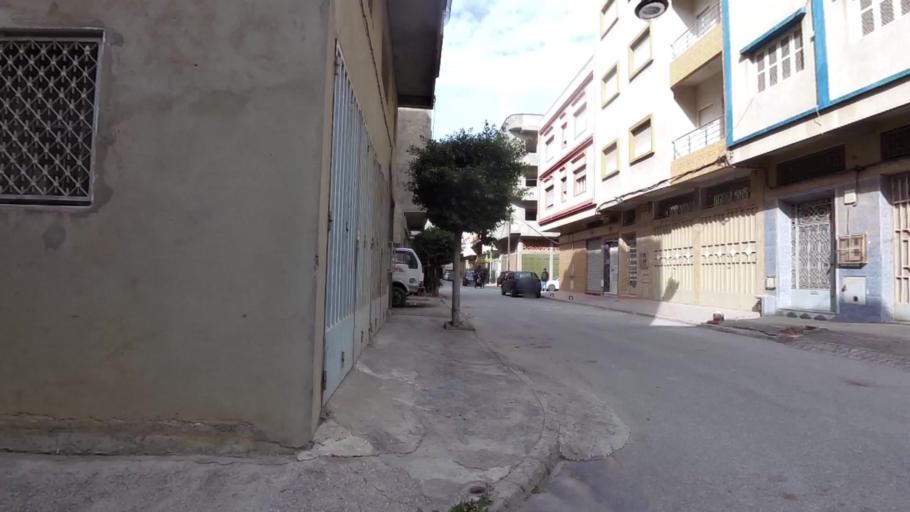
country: MA
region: Tanger-Tetouan
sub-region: Tanger-Assilah
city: Tangier
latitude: 35.7537
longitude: -5.7943
